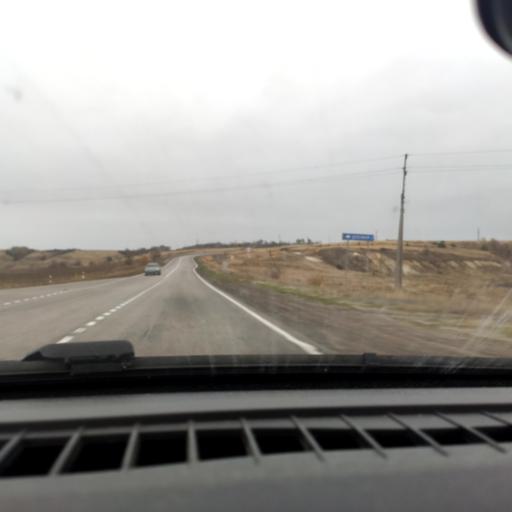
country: RU
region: Voronezj
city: Uryv-Pokrovka
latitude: 51.1323
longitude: 39.0454
